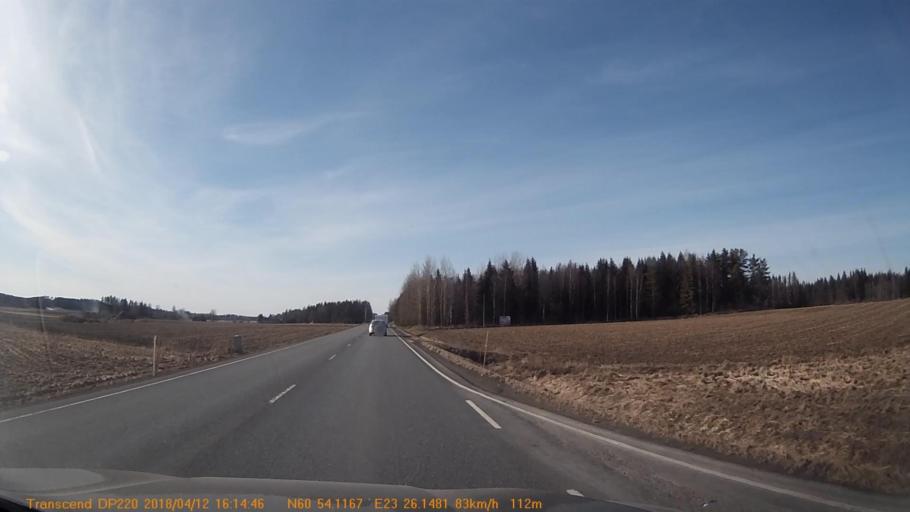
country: FI
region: Haeme
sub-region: Forssa
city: Humppila
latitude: 60.9021
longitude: 23.4356
